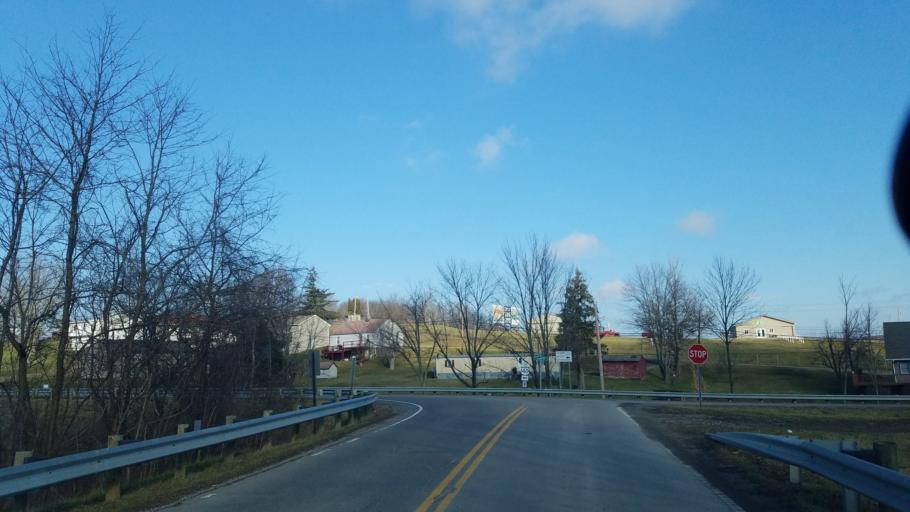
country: US
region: Ohio
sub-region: Guernsey County
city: Byesville
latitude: 40.0358
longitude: -81.4343
